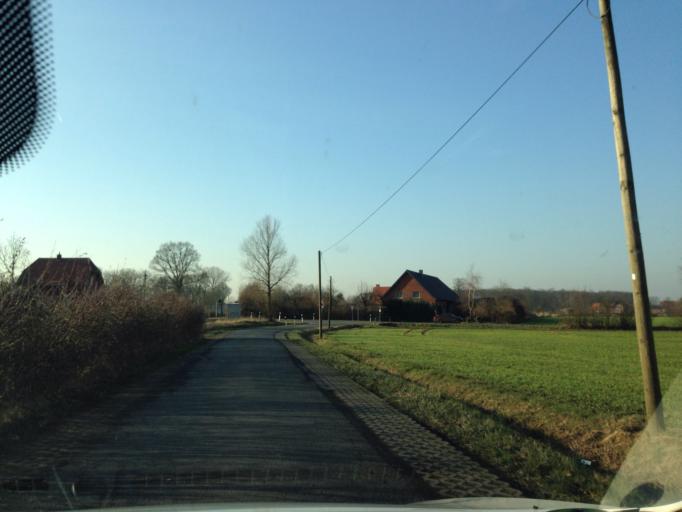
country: DE
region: North Rhine-Westphalia
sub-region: Regierungsbezirk Munster
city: Muenster
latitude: 52.0182
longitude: 7.5766
